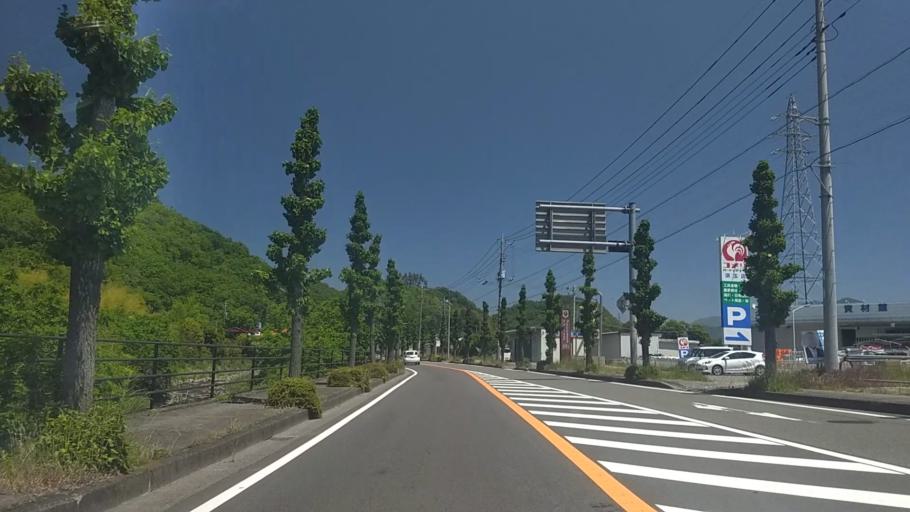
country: JP
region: Yamanashi
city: Nirasaki
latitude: 35.7867
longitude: 138.4187
